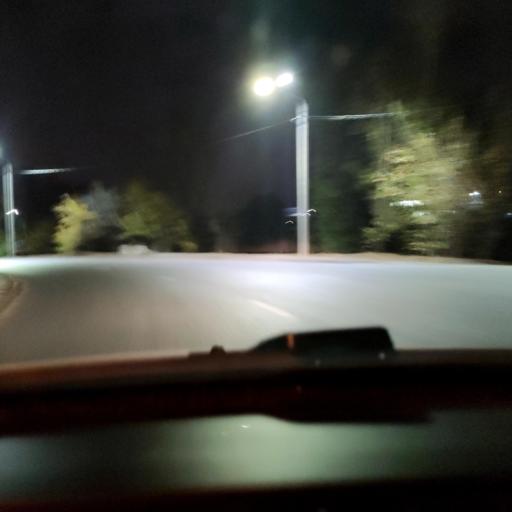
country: RU
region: Voronezj
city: Maslovka
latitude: 51.6224
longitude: 39.2618
